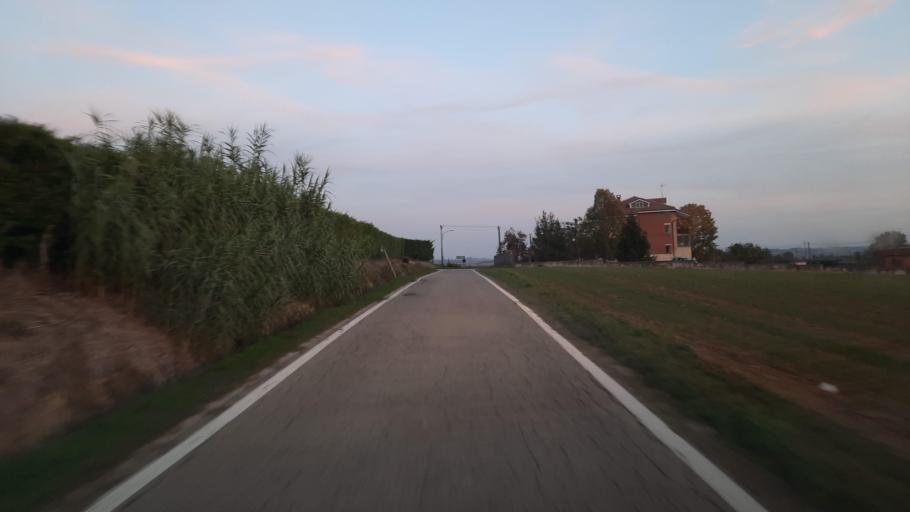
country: IT
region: Piedmont
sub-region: Provincia di Asti
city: Tonco
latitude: 45.0199
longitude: 8.2020
